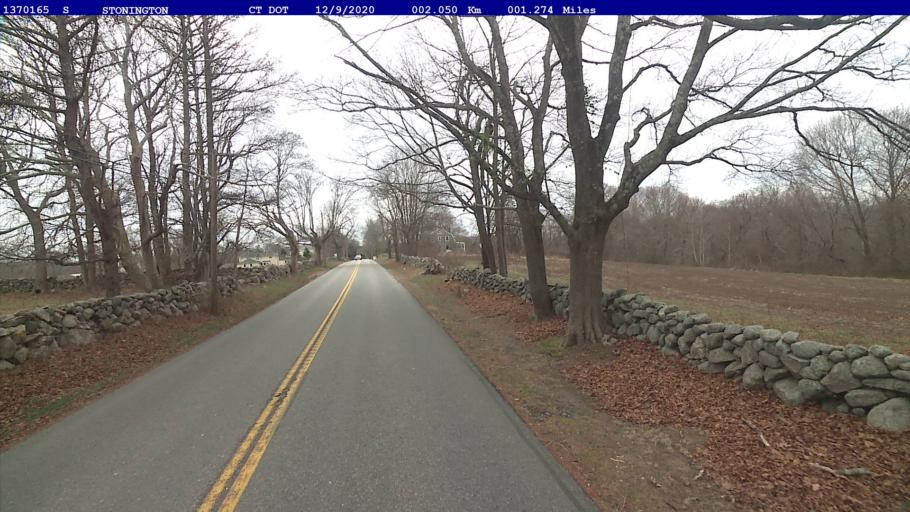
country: US
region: Connecticut
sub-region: New London County
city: Mystic
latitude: 41.3550
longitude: -71.9036
